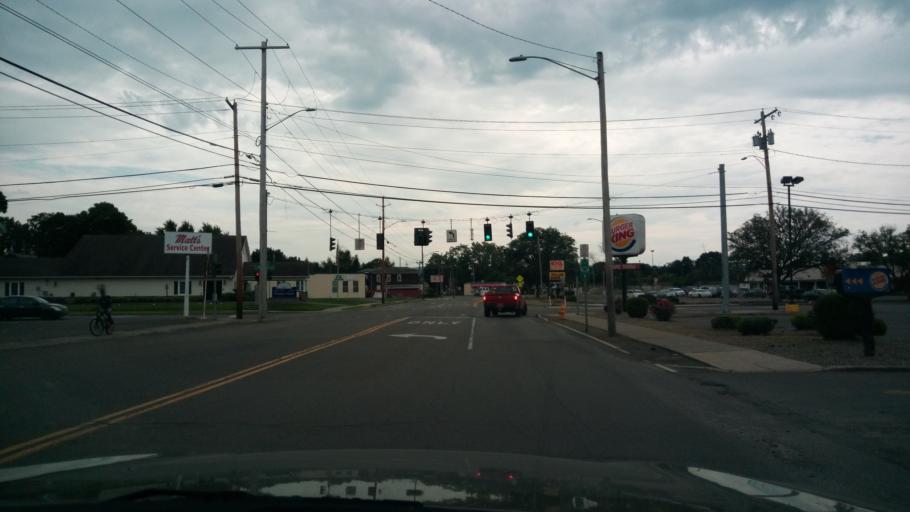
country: US
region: New York
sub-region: Chemung County
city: Elmira
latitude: 42.1023
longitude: -76.8045
